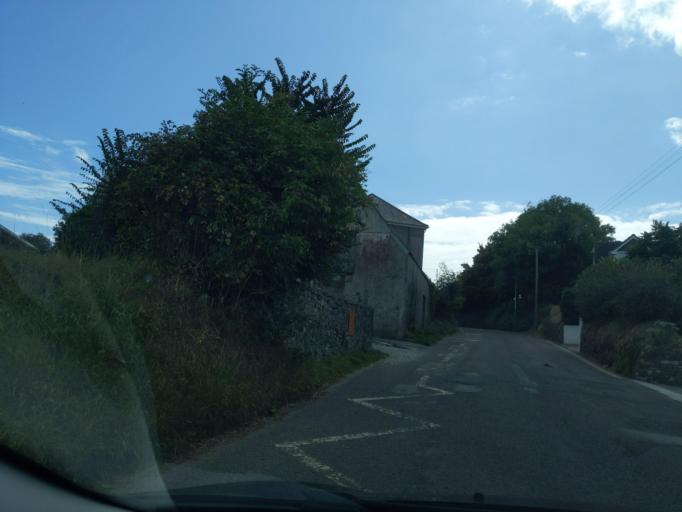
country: GB
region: England
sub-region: Devon
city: Modbury
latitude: 50.3511
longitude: -3.8894
